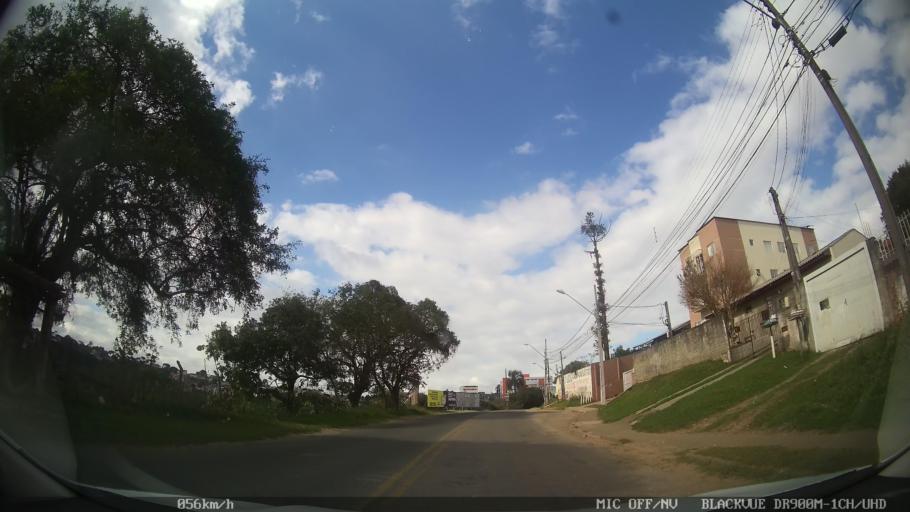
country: BR
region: Parana
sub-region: Colombo
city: Colombo
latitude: -25.3611
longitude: -49.2046
